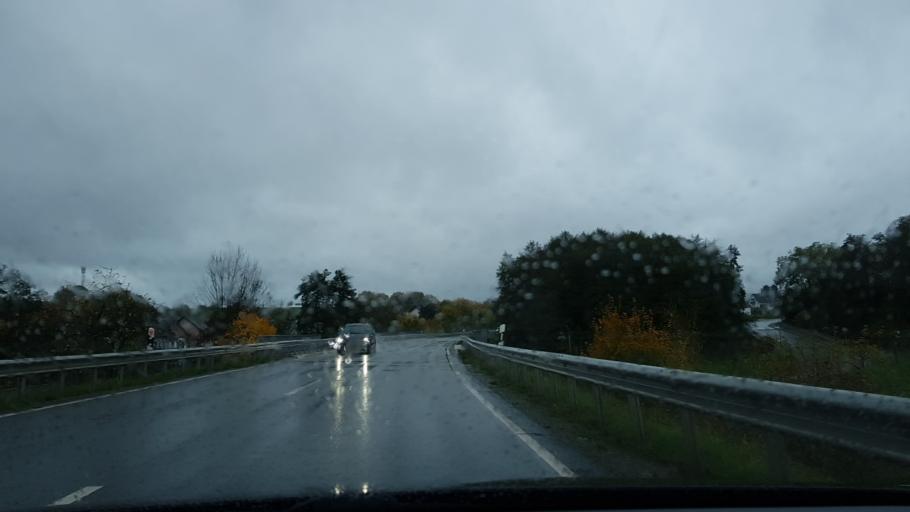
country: DE
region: Rheinland-Pfalz
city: Salmtal
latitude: 49.9266
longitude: 6.8414
